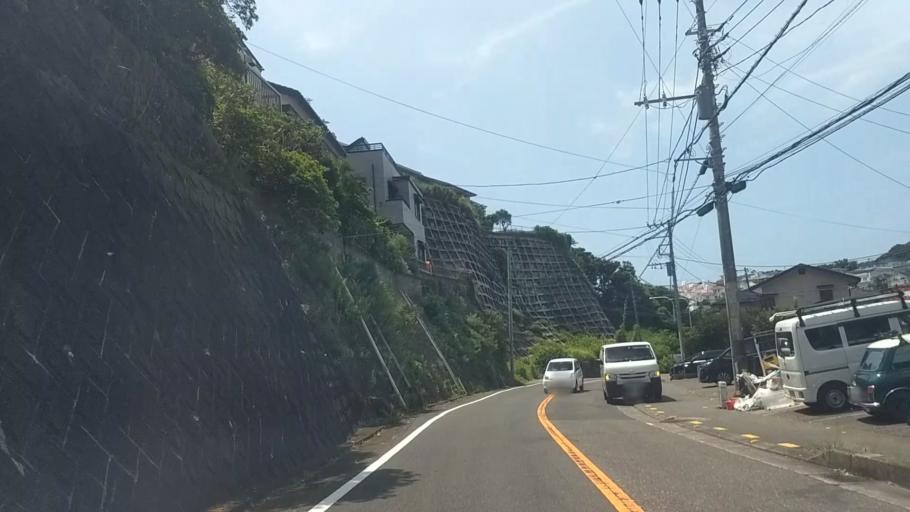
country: JP
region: Kanagawa
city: Kamakura
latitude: 35.3034
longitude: 139.5612
